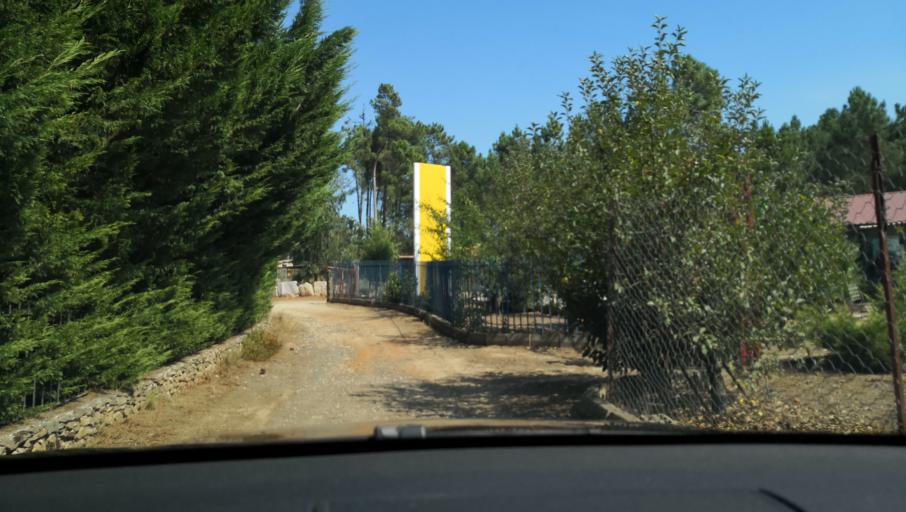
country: PT
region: Vila Real
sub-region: Sabrosa
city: Vilela
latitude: 41.2621
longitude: -7.6285
